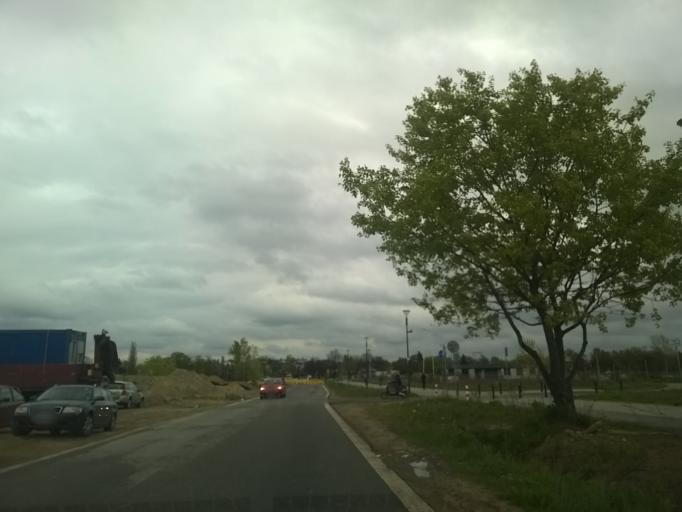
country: PL
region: Masovian Voivodeship
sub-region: Warszawa
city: Wilanow
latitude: 52.1588
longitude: 21.0845
